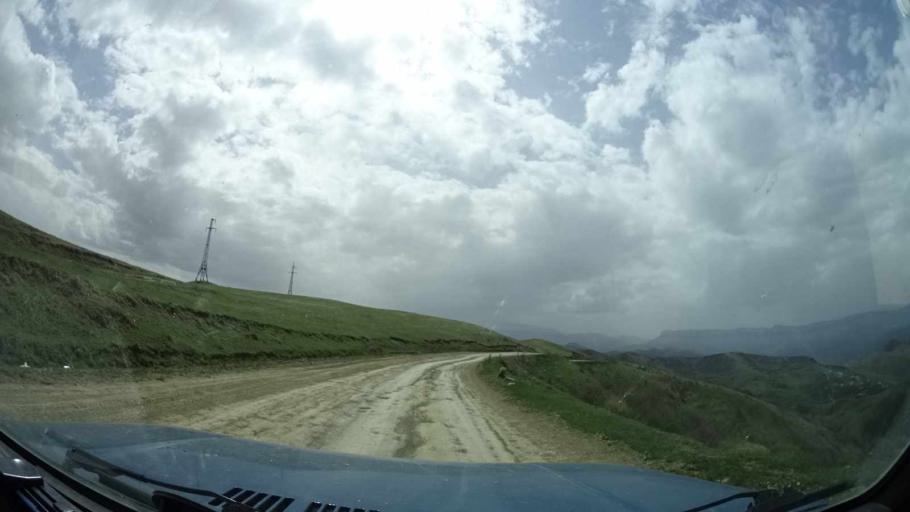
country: RU
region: Dagestan
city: Kubachi
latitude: 42.0872
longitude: 47.5755
